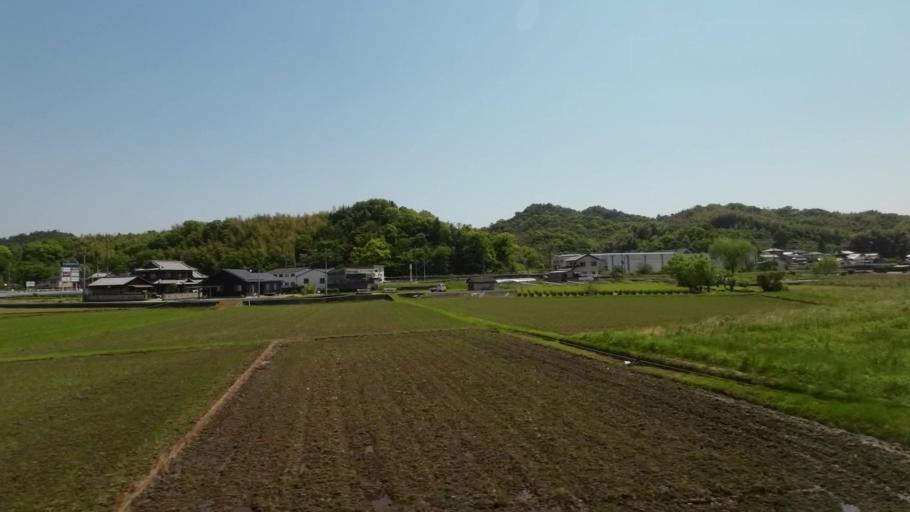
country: JP
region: Ehime
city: Saijo
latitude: 34.0028
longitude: 133.0368
